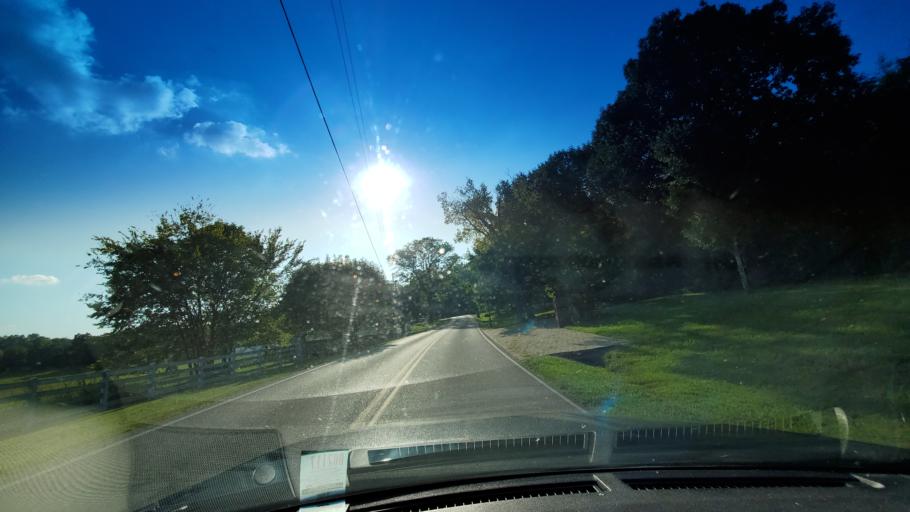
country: US
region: Tennessee
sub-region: Wilson County
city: Lebanon
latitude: 36.1650
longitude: -86.3704
